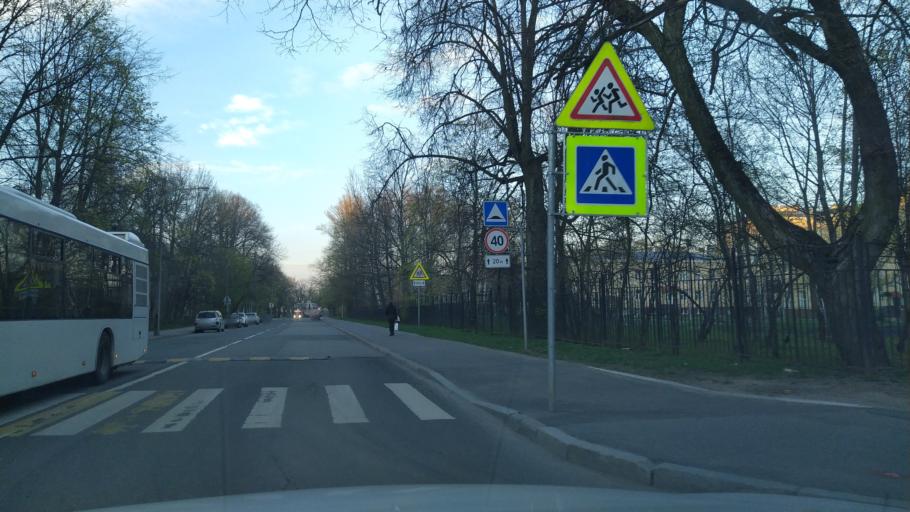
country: RU
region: St.-Petersburg
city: Pushkin
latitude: 59.7078
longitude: 30.4090
